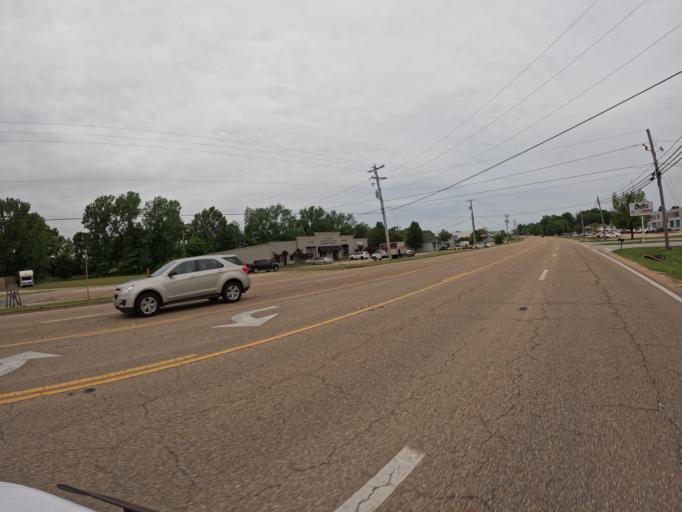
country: US
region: Mississippi
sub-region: Lee County
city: Tupelo
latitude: 34.2895
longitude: -88.7464
